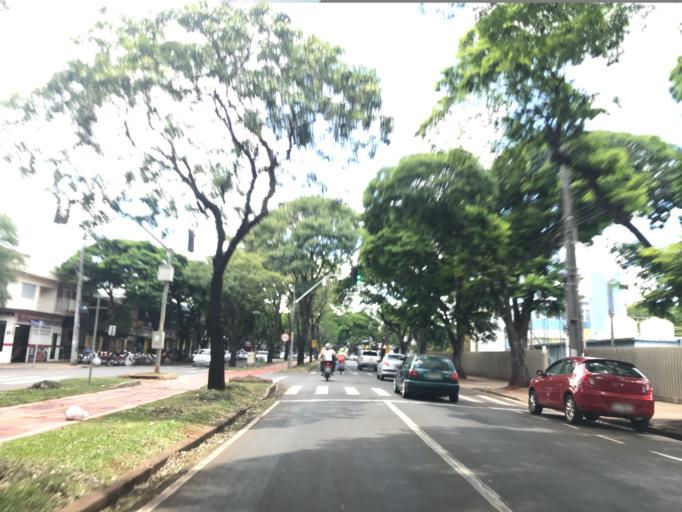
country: BR
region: Parana
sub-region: Maringa
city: Maringa
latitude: -23.4101
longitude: -51.9241
